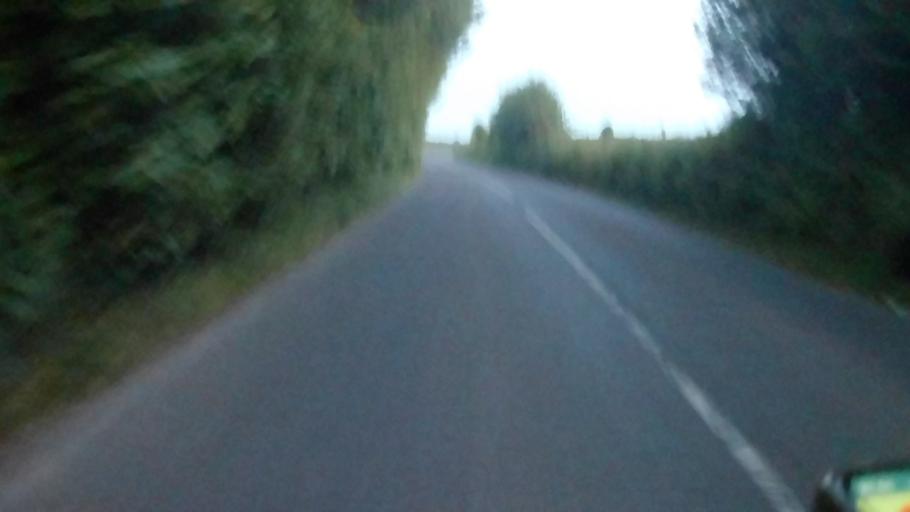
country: IE
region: Munster
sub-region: County Cork
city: Carrigtwohill
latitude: 51.9538
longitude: -8.3048
